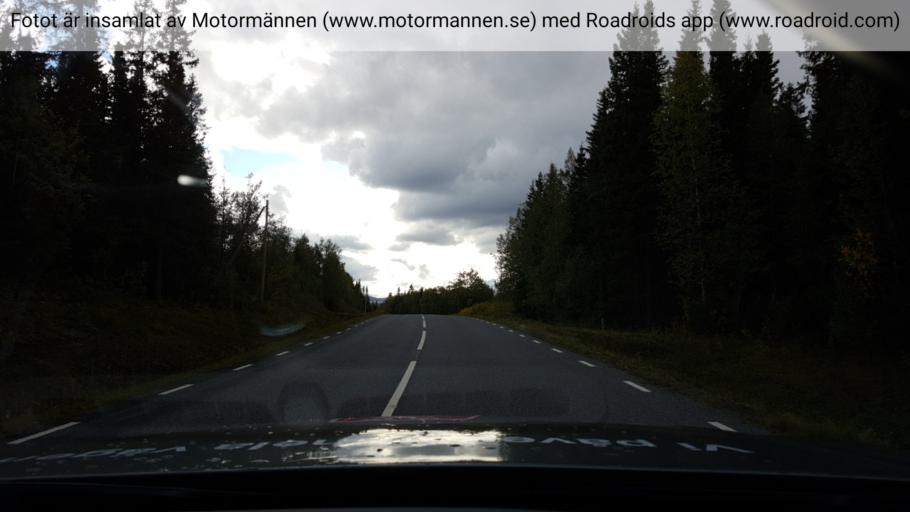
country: SE
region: Jaemtland
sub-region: Are Kommun
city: Are
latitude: 63.5860
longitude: 13.0231
